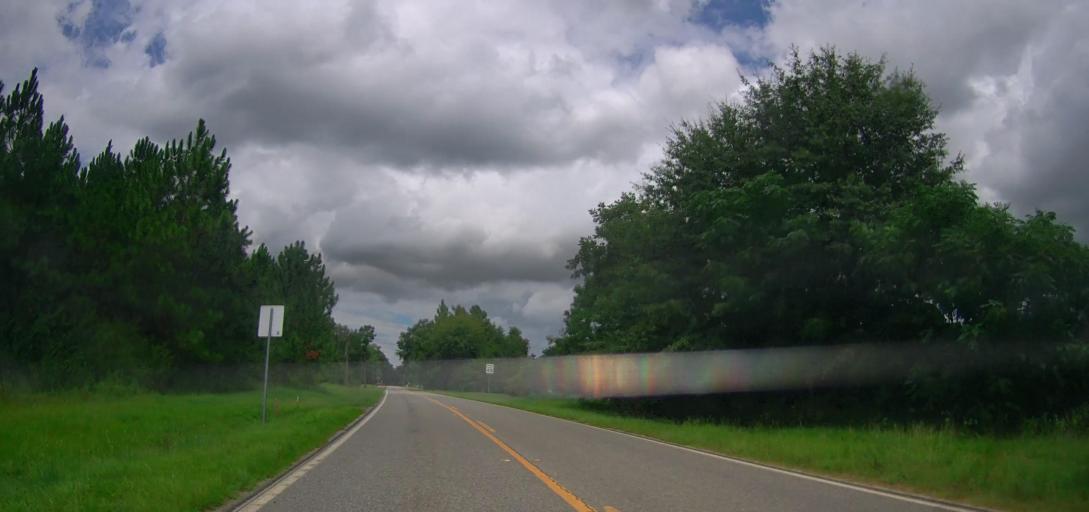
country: US
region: Georgia
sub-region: Wilcox County
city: Rochelle
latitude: 31.9391
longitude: -83.5427
